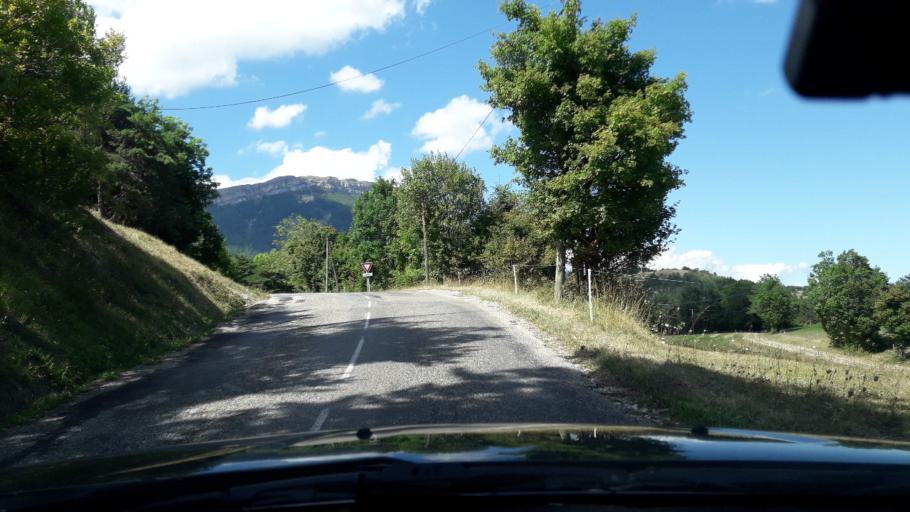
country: FR
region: Rhone-Alpes
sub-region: Departement de l'Isere
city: Mens
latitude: 44.8498
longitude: 5.6223
